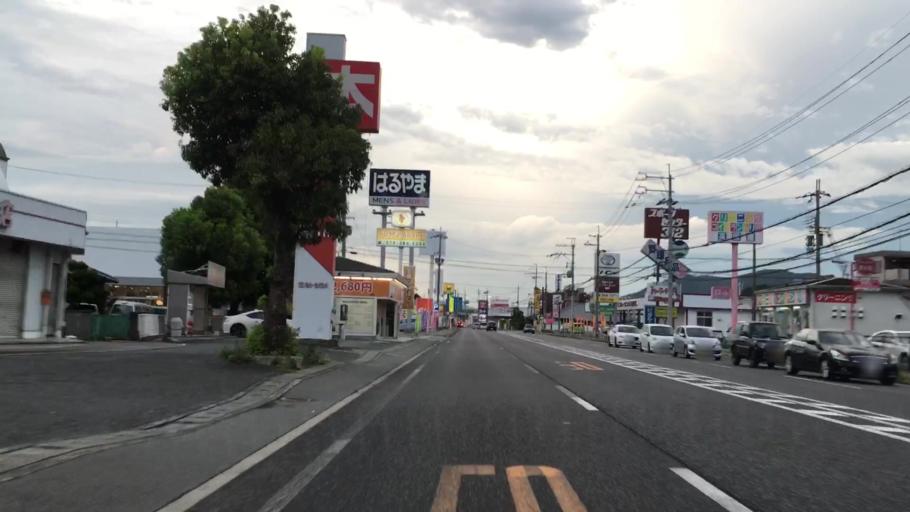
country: JP
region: Hyogo
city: Himeji
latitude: 34.8657
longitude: 134.7269
